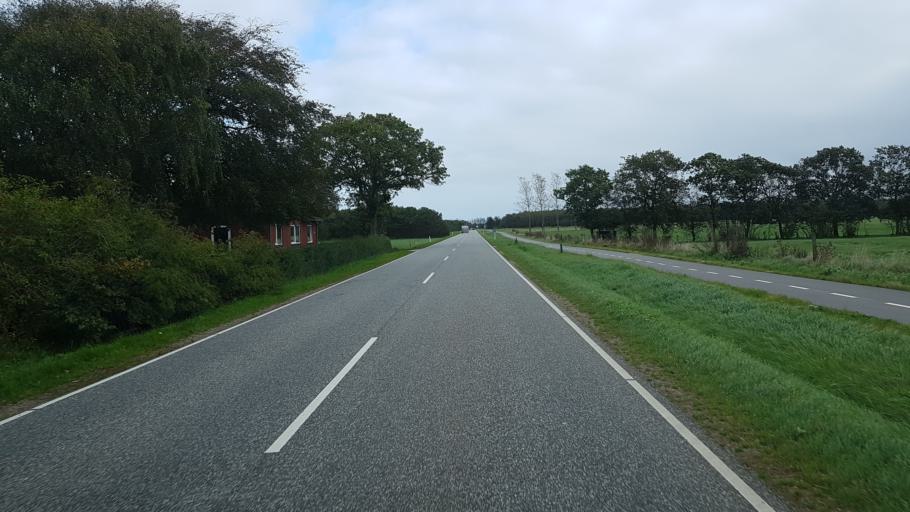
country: DK
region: South Denmark
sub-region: Billund Kommune
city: Grindsted
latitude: 55.7644
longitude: 8.8535
